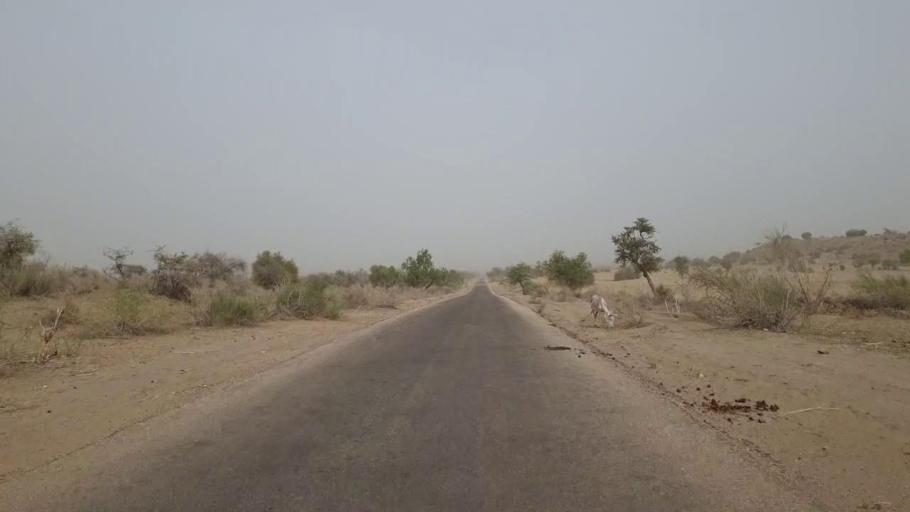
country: PK
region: Sindh
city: Islamkot
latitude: 24.5793
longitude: 70.3058
